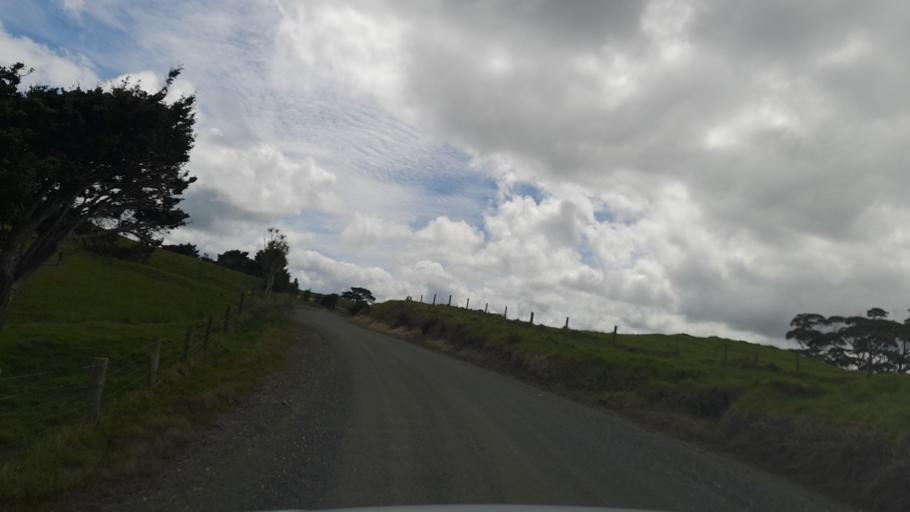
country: NZ
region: Auckland
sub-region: Auckland
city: Wellsford
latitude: -36.2039
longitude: 174.3371
